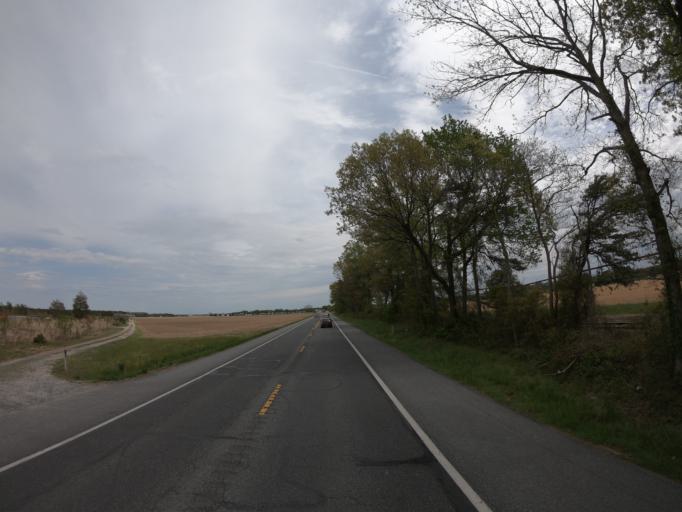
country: US
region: Delaware
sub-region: Sussex County
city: Milton
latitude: 38.7868
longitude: -75.3632
